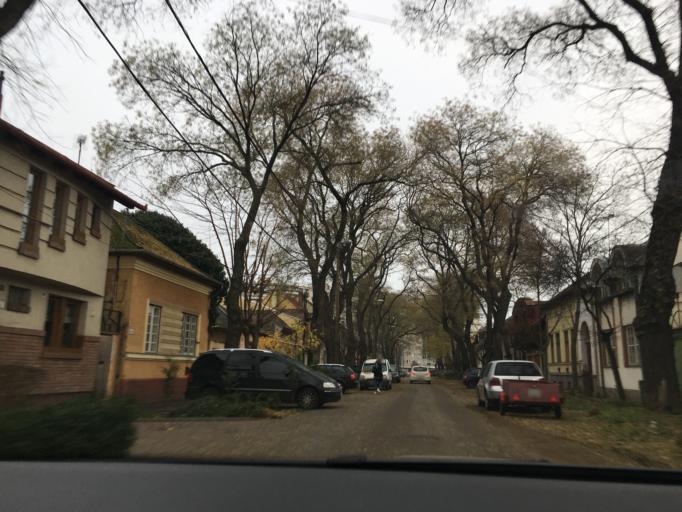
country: HU
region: Hajdu-Bihar
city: Debrecen
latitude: 47.5348
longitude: 21.6383
